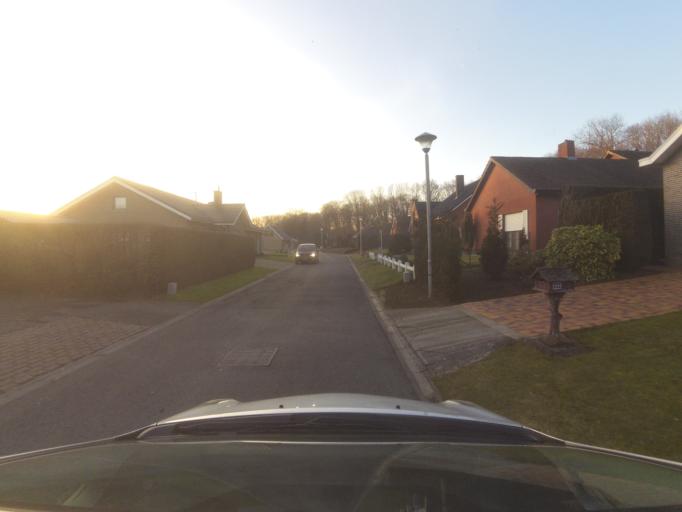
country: BE
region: Flanders
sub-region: Provincie West-Vlaanderen
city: Ieper
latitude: 50.8817
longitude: 2.8187
